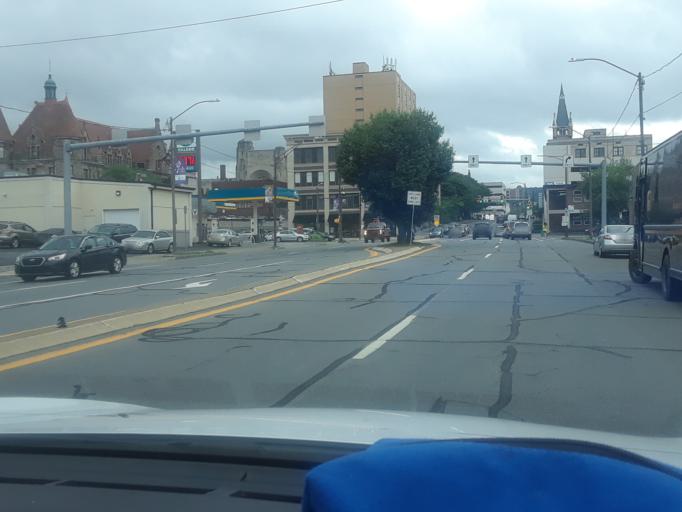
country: US
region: Pennsylvania
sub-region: Lackawanna County
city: Scranton
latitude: 41.4118
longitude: -75.6636
